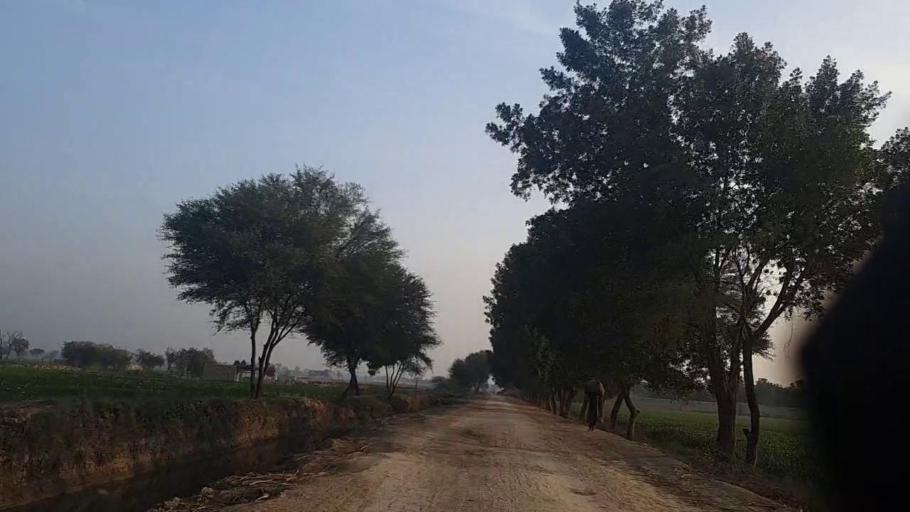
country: PK
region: Sindh
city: Sakrand
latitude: 26.1193
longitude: 68.2318
